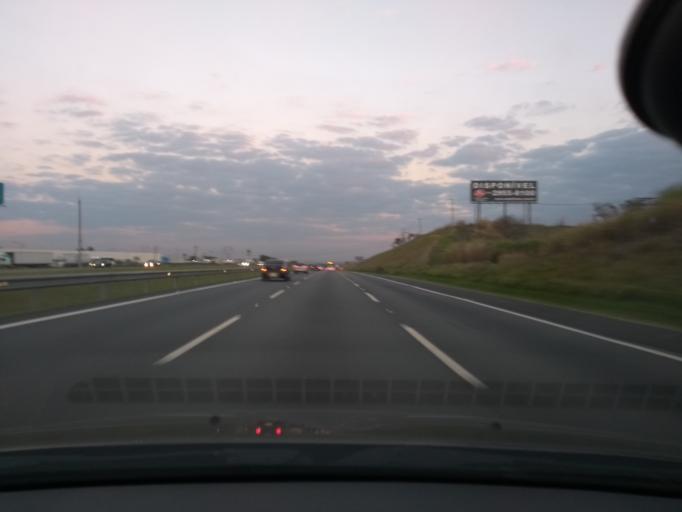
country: BR
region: Sao Paulo
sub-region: Louveira
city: Louveira
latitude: -23.1171
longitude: -46.9949
